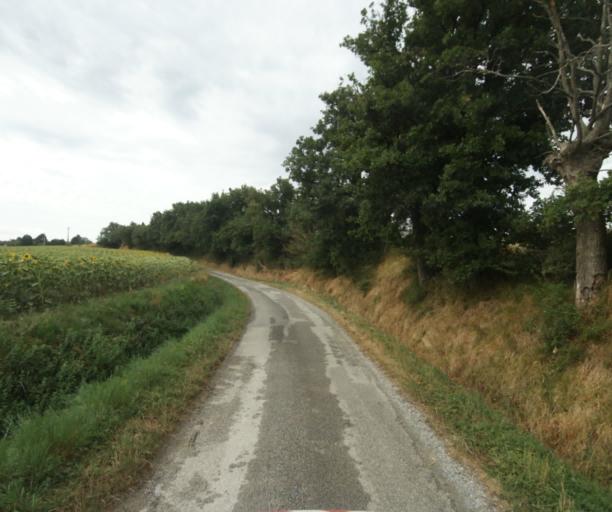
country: FR
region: Midi-Pyrenees
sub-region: Departement de la Haute-Garonne
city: Revel
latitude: 43.4326
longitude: 1.9668
